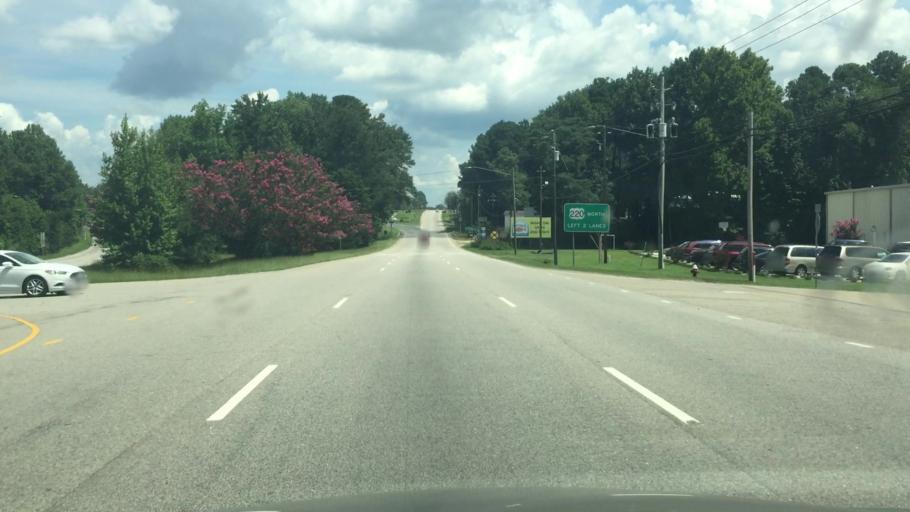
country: US
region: North Carolina
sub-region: Richmond County
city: Rockingham
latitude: 34.9228
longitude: -79.7817
